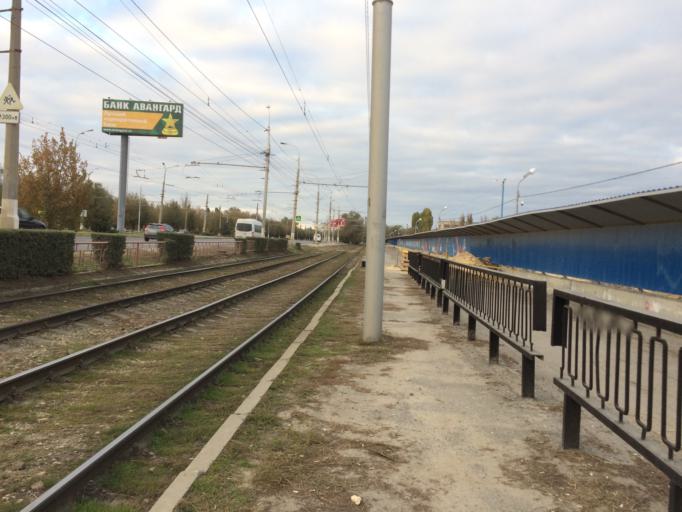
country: RU
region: Volgograd
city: Krasnoslobodsk
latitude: 48.7350
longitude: 44.5440
